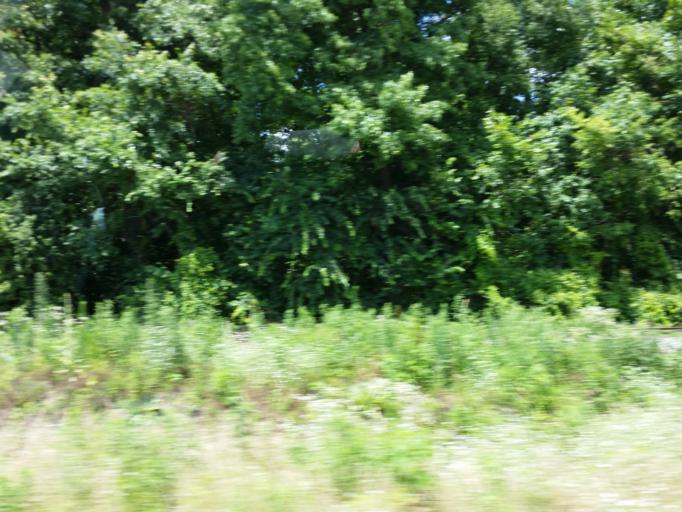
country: US
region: Tennessee
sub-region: Lake County
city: Tiptonville
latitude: 36.4917
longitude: -89.3671
